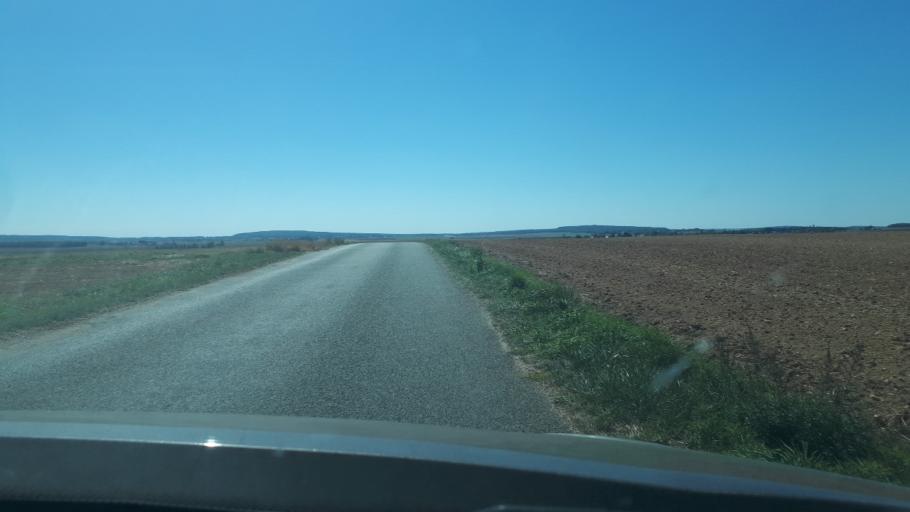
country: FR
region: Centre
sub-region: Departement du Cher
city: Baugy
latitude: 47.2174
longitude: 2.7507
